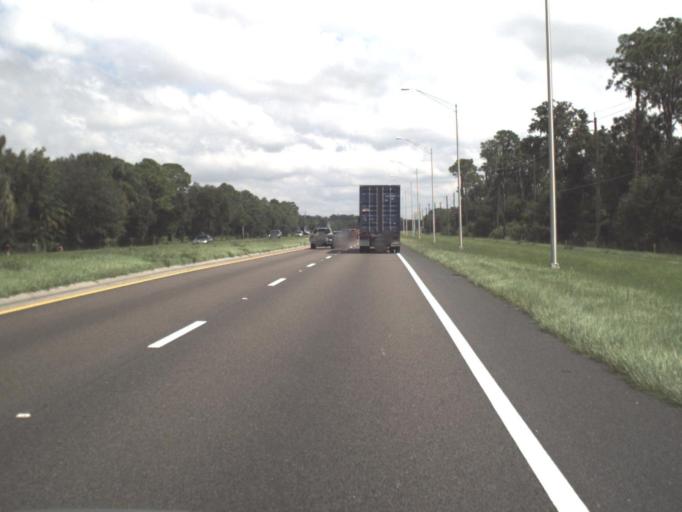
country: US
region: Florida
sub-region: Manatee County
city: Ellenton
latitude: 27.4841
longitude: -82.4184
